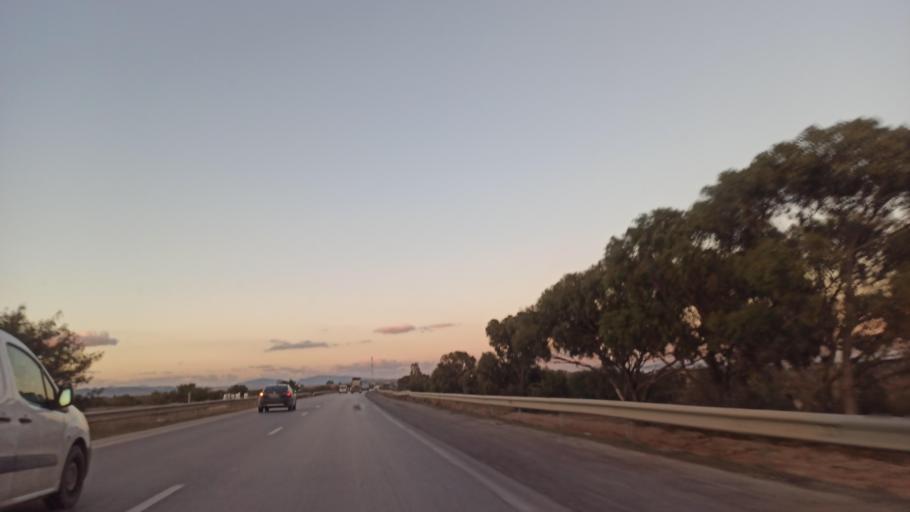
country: TN
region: Nabul
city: Al Hammamat
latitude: 36.2578
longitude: 10.4277
